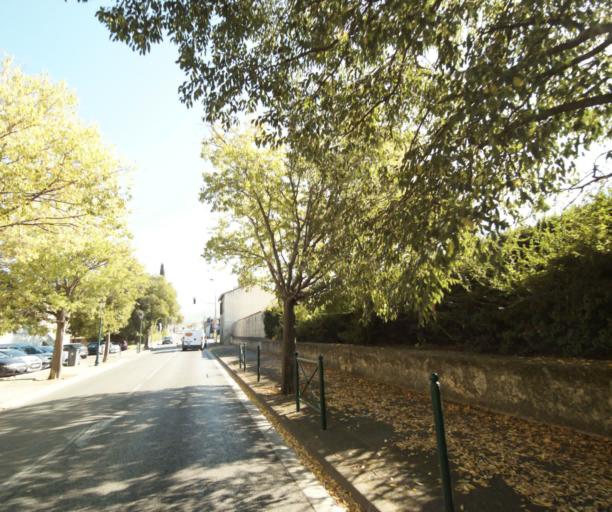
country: FR
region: Provence-Alpes-Cote d'Azur
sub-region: Departement des Bouches-du-Rhone
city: Plan-de-Cuques
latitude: 43.3487
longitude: 5.4669
